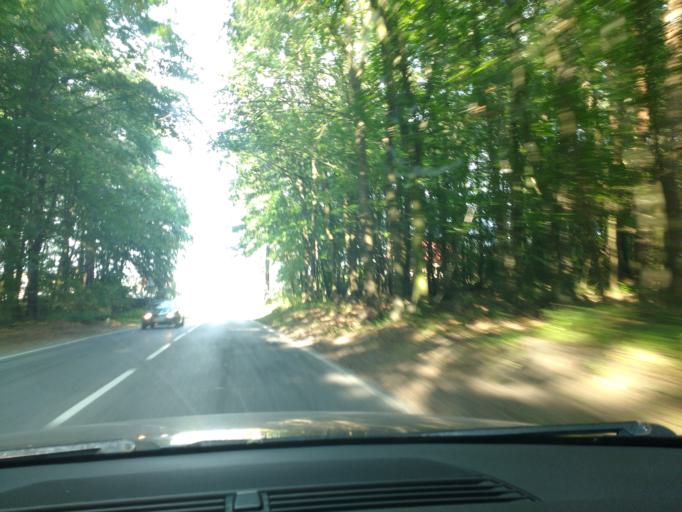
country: PL
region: Pomeranian Voivodeship
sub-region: Gdynia
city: Wielki Kack
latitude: 54.4644
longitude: 18.5088
